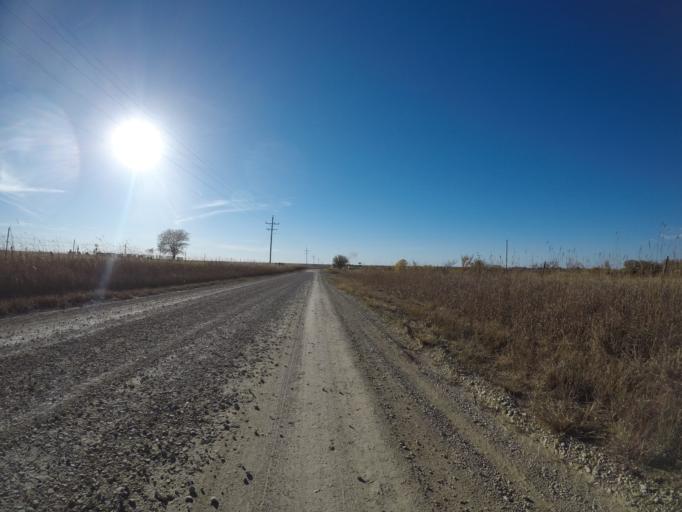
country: US
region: Kansas
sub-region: Riley County
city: Ogden
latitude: 39.2615
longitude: -96.7185
